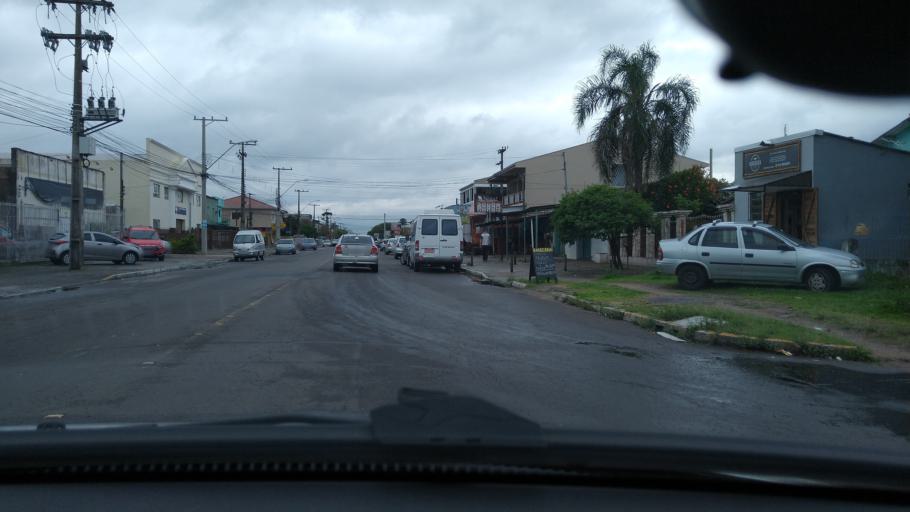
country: BR
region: Rio Grande do Sul
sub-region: Canoas
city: Canoas
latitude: -29.9015
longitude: -51.2142
